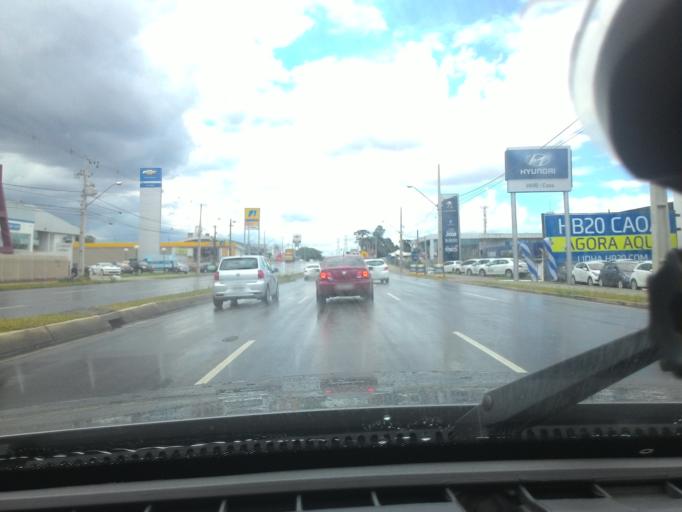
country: BR
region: Parana
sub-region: Sao Jose Dos Pinhais
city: Sao Jose dos Pinhais
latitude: -25.5196
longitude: -49.1993
